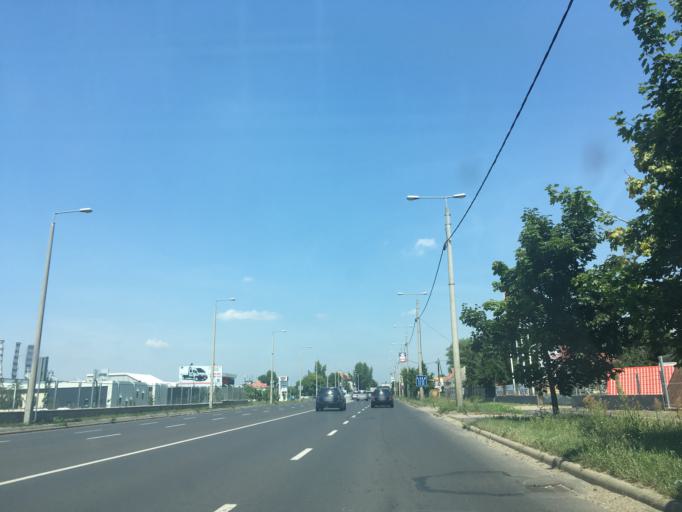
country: HU
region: Hajdu-Bihar
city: Debrecen
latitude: 47.5008
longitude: 21.6312
